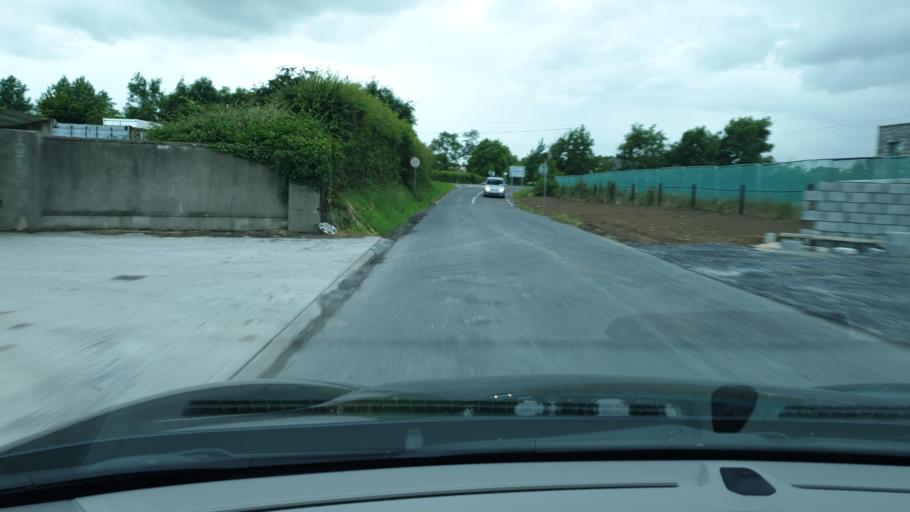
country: IE
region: Leinster
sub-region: An Mhi
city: Navan
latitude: 53.6244
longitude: -6.7047
